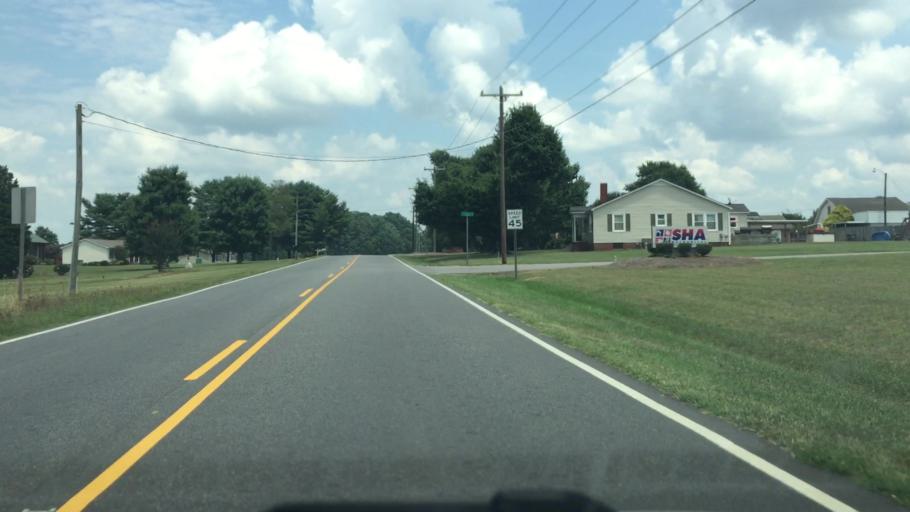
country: US
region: North Carolina
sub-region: Iredell County
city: Troutman
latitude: 35.7183
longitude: -80.8811
